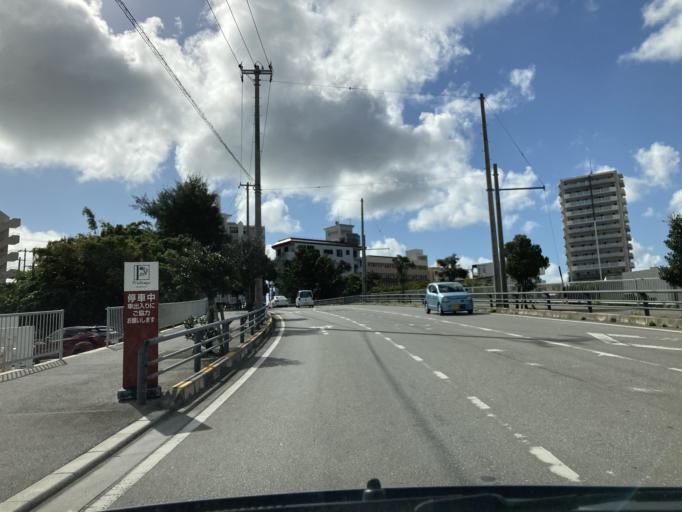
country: JP
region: Okinawa
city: Ginowan
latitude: 26.2335
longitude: 127.7244
